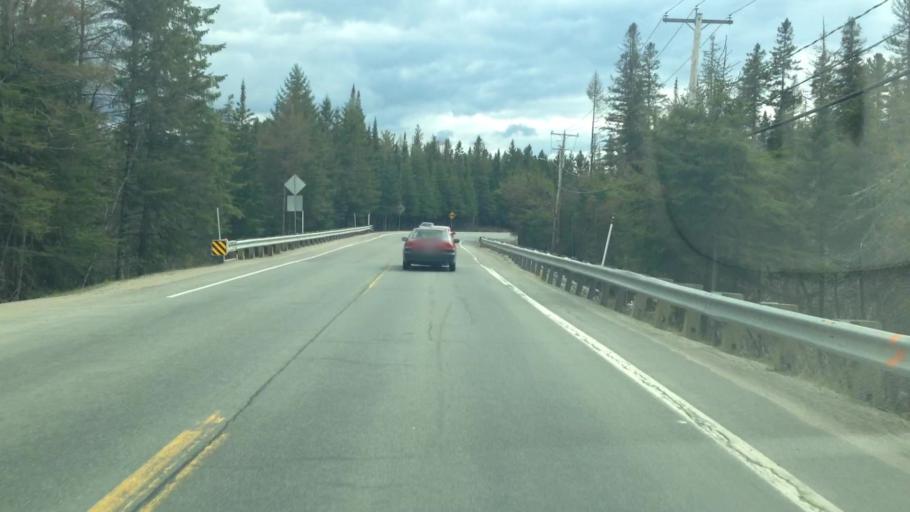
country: CA
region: Quebec
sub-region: Laurentides
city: Sainte-Adele
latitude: 46.0165
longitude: -74.0973
